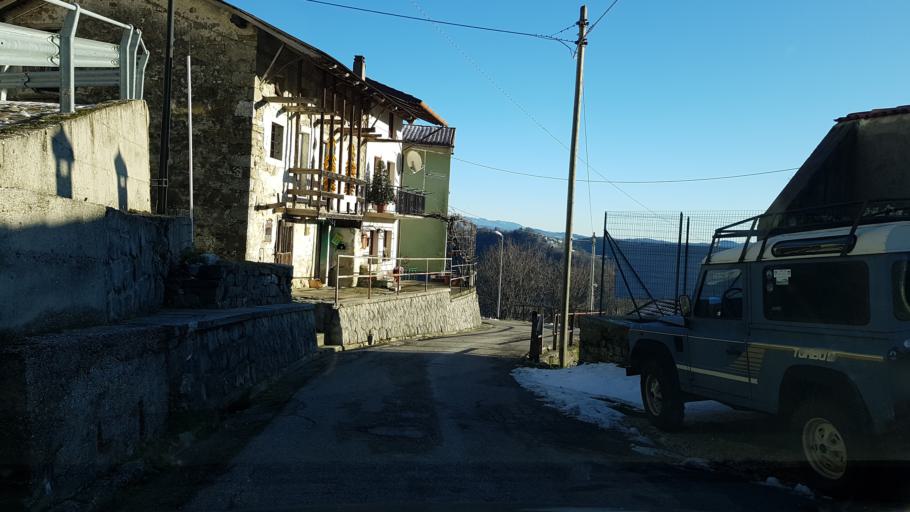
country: IT
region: Friuli Venezia Giulia
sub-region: Provincia di Udine
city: Savogna
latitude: 46.1872
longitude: 13.5323
